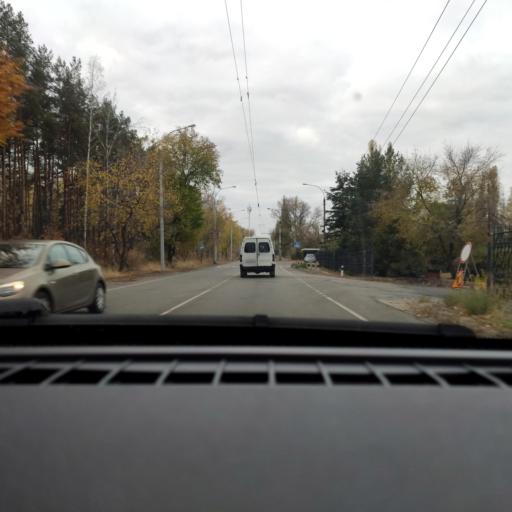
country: RU
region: Voronezj
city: Somovo
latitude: 51.7139
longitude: 39.2932
